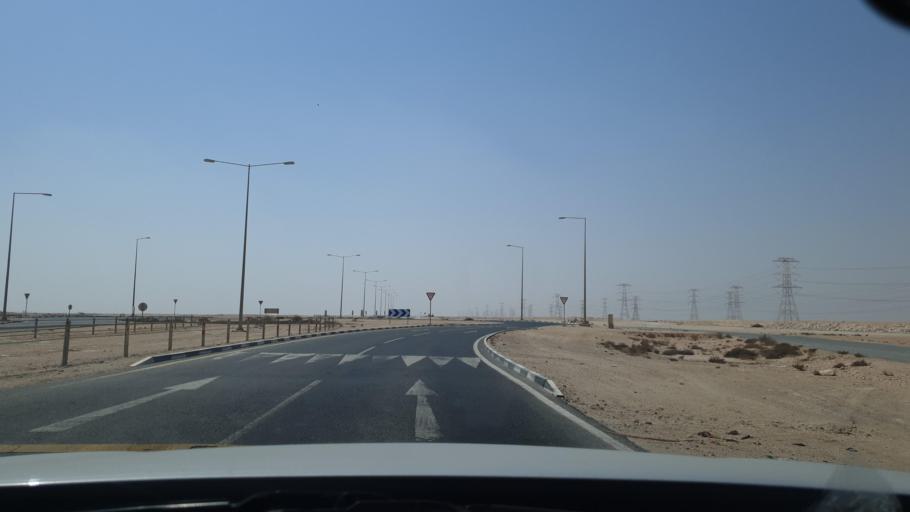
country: QA
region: Al Khawr
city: Al Khawr
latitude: 25.7327
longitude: 51.4575
